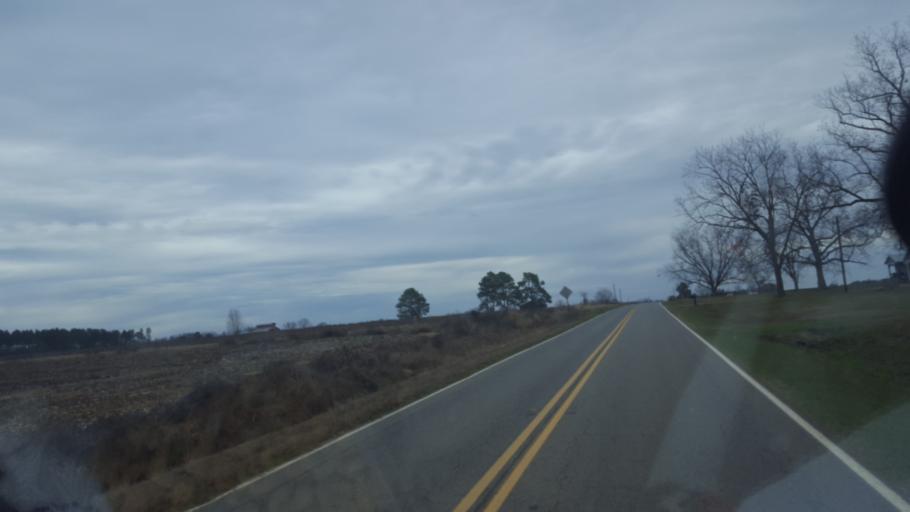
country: US
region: Georgia
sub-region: Ben Hill County
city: Fitzgerald
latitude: 31.7439
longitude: -83.3164
